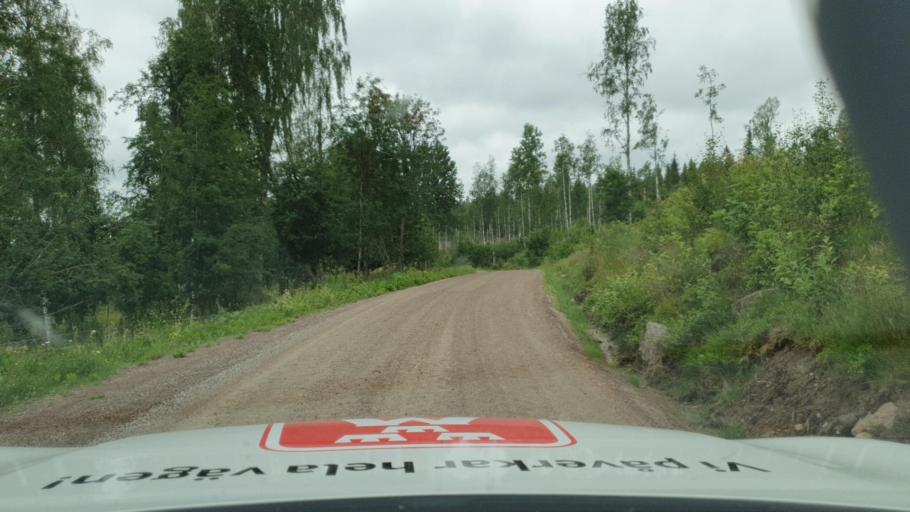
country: SE
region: Vaermland
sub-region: Filipstads Kommun
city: Filipstad
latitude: 59.5692
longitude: 13.9646
